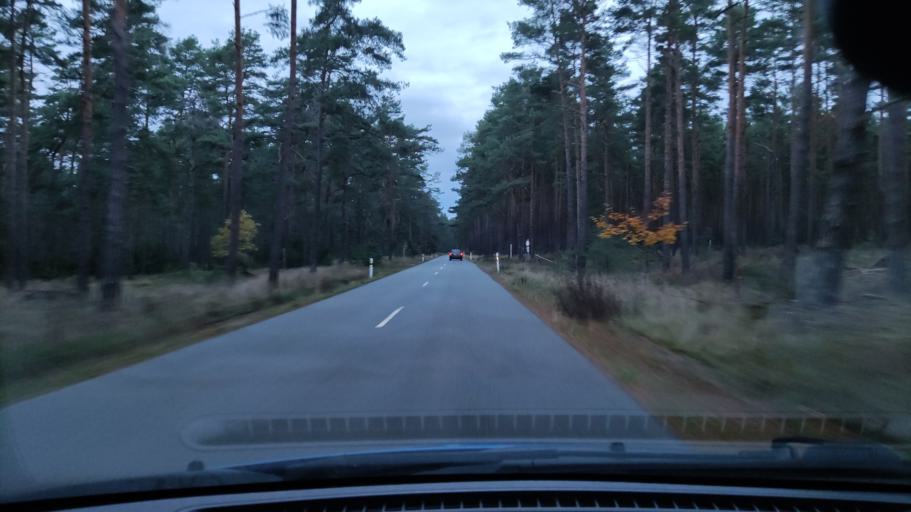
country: DE
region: Lower Saxony
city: Gorleben
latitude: 53.0146
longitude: 11.3886
